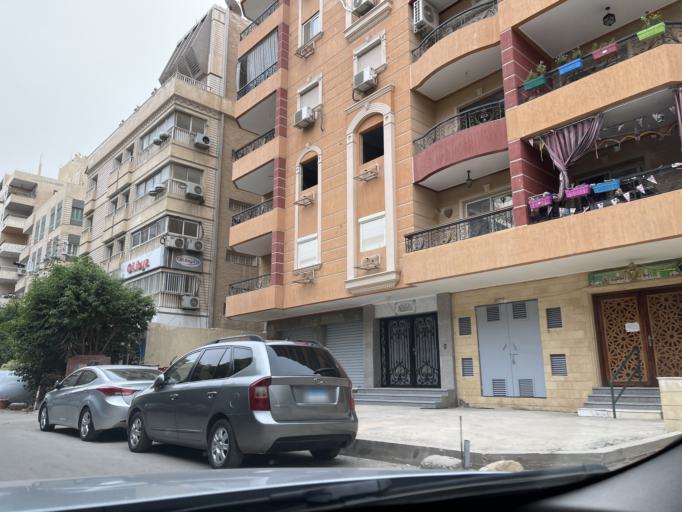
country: EG
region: Muhafazat al Qahirah
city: Cairo
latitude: 30.0594
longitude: 31.3511
